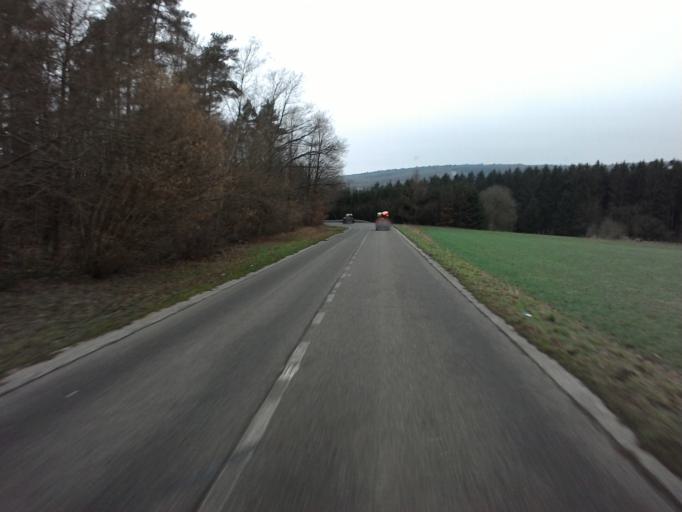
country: BE
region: Wallonia
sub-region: Province de Namur
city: Gedinne
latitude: 50.0382
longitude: 4.9413
